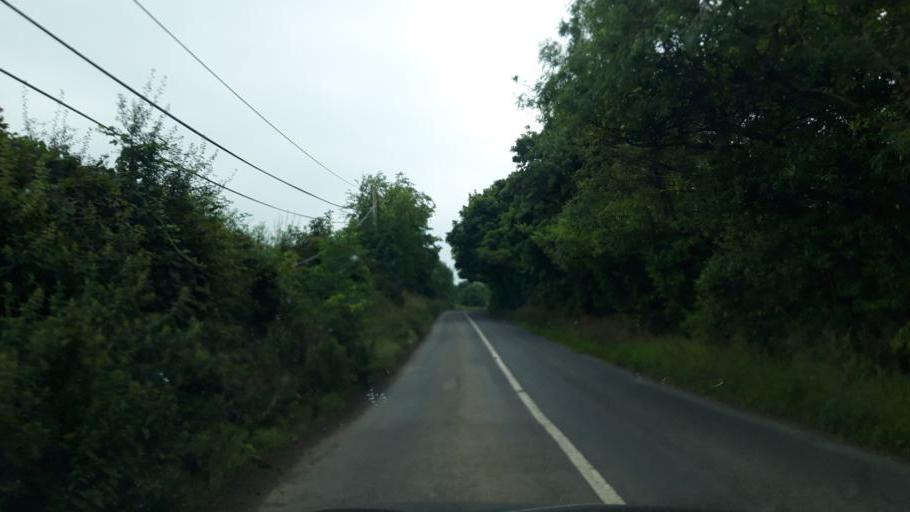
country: IE
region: Munster
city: Fethard
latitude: 52.5333
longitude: -7.6804
